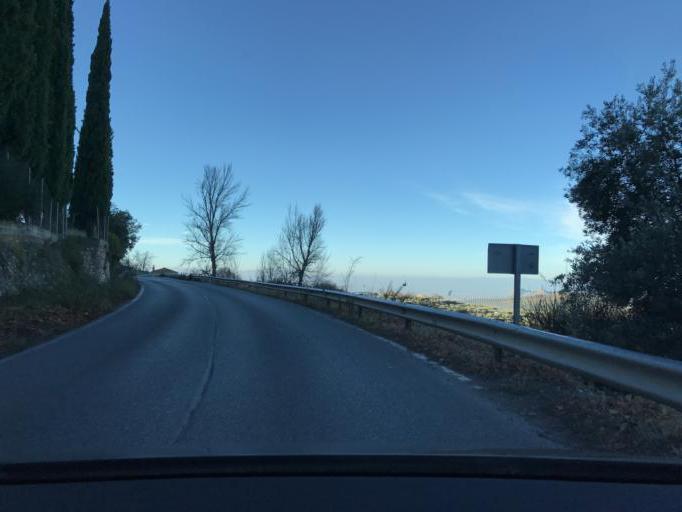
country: ES
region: Andalusia
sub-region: Provincia de Granada
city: Nivar
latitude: 37.2658
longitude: -3.5851
